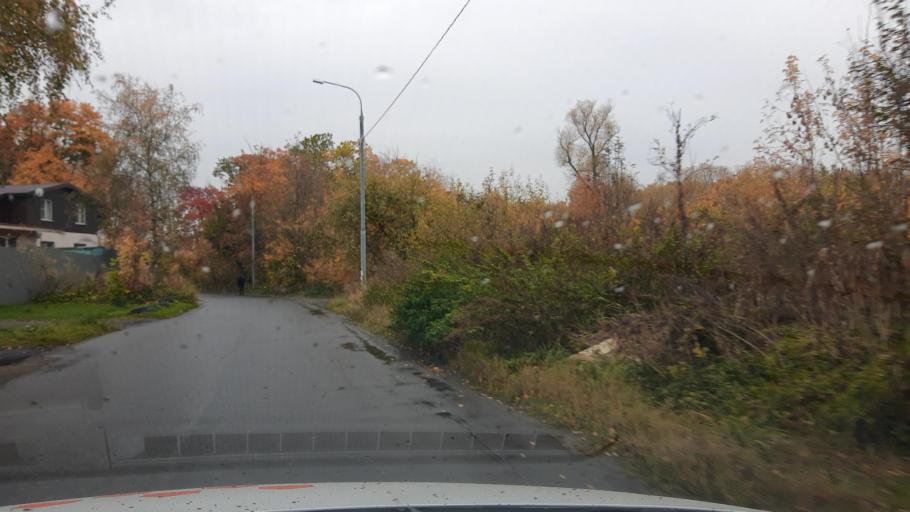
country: RU
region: Moskovskaya
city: Shcherbinka
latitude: 55.5390
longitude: 37.5660
